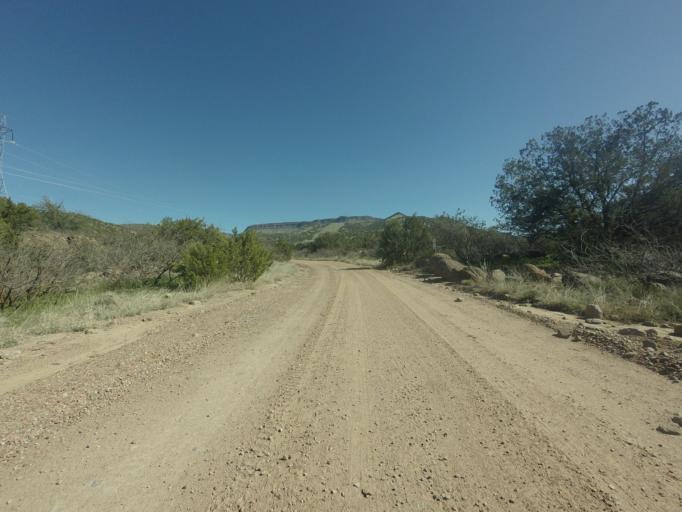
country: US
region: Arizona
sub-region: Gila County
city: Pine
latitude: 34.3911
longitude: -111.6510
